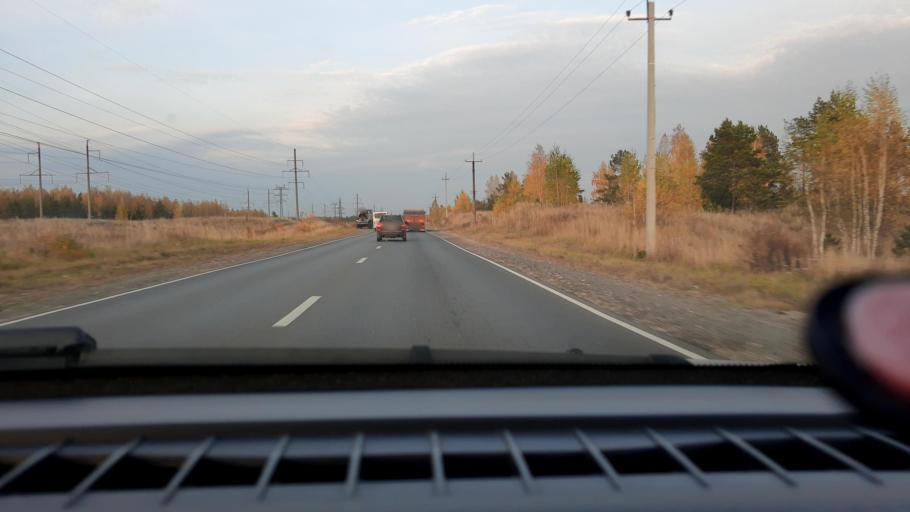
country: RU
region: Nizjnij Novgorod
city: Babino
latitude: 56.3312
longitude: 43.5669
